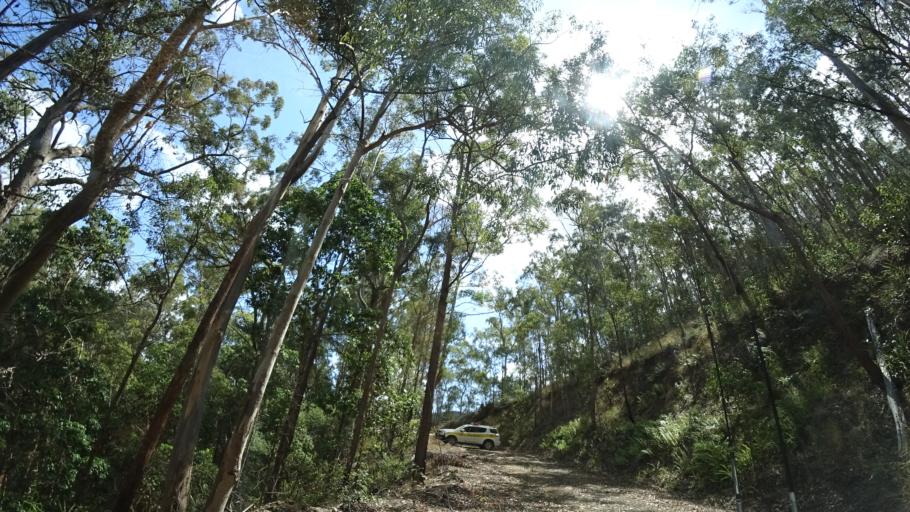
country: AU
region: Queensland
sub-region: Moreton Bay
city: Highvale
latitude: -27.3449
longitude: 152.7245
